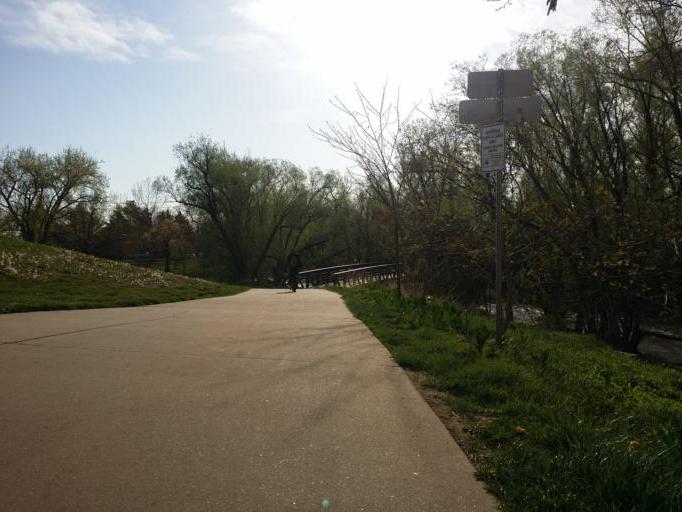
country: US
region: Colorado
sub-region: Boulder County
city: Boulder
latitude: 40.0110
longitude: -105.2553
